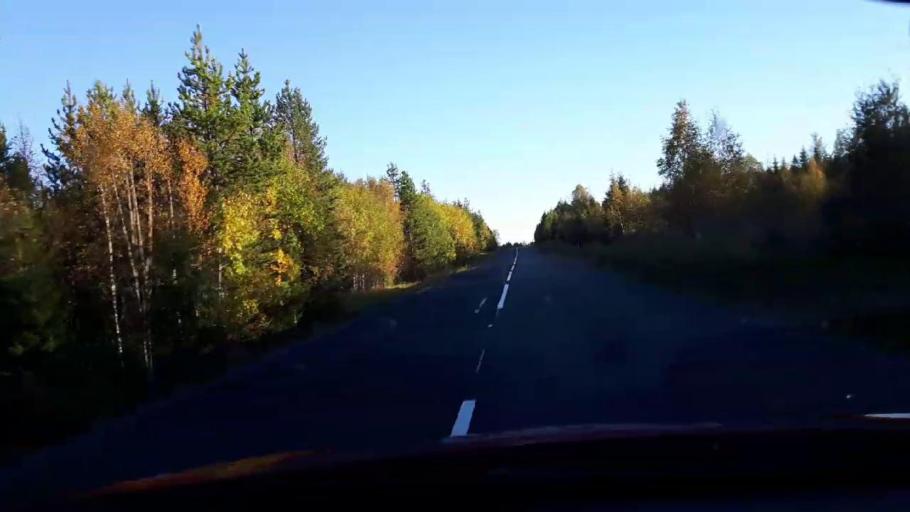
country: SE
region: Jaemtland
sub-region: OEstersunds Kommun
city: Lit
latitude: 63.4825
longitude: 14.8802
